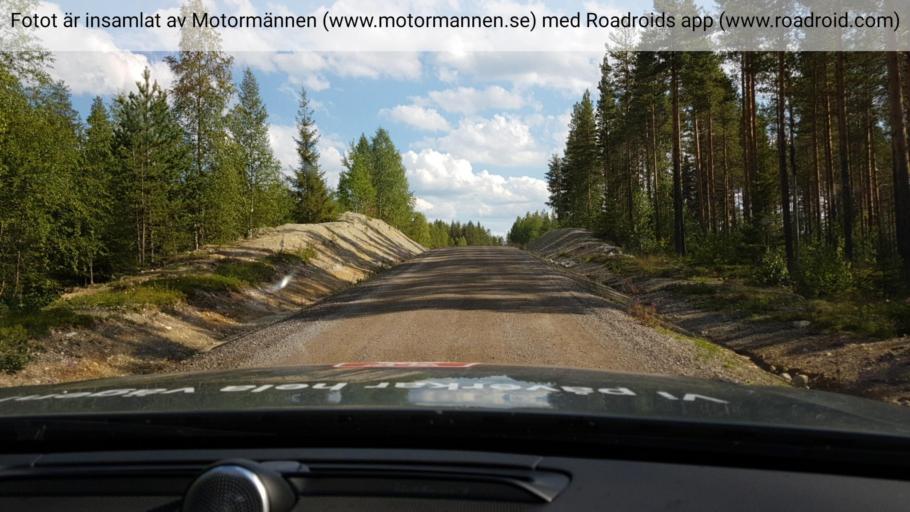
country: SE
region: Vaesterbotten
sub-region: Dorotea Kommun
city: Dorotea
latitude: 63.9638
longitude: 16.0726
